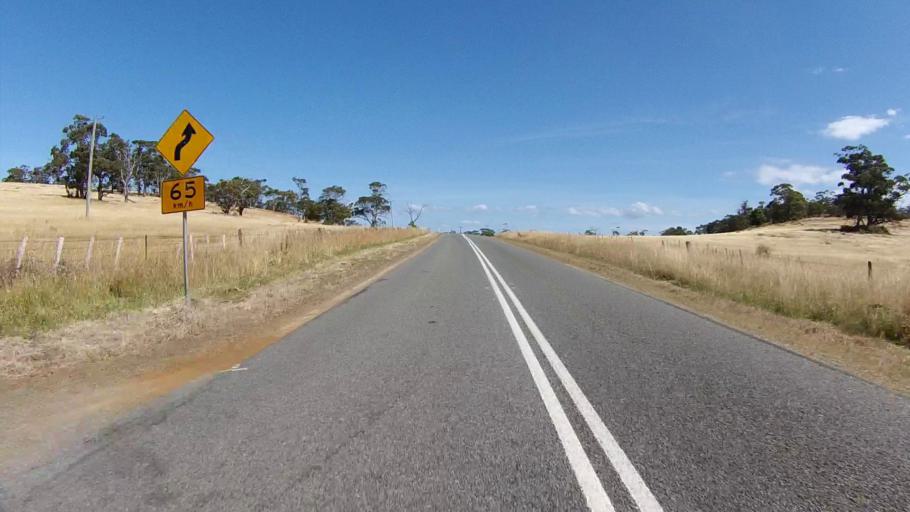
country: AU
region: Tasmania
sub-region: Sorell
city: Sorell
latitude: -42.2991
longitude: 147.9821
